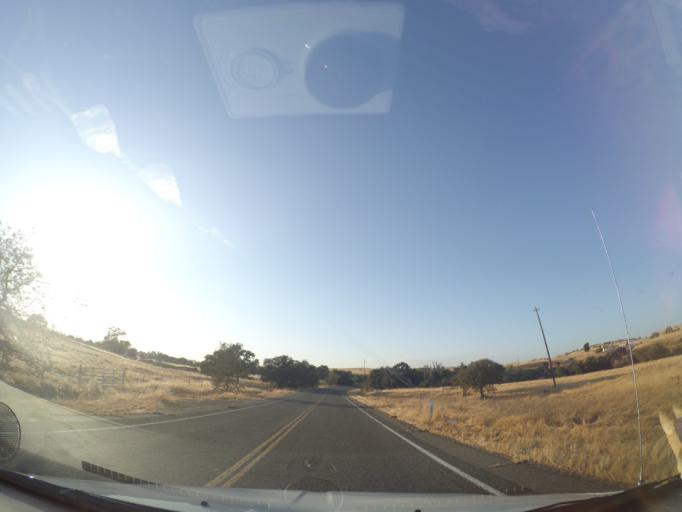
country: US
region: California
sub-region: Merced County
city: Planada
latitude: 37.5219
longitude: -120.3198
